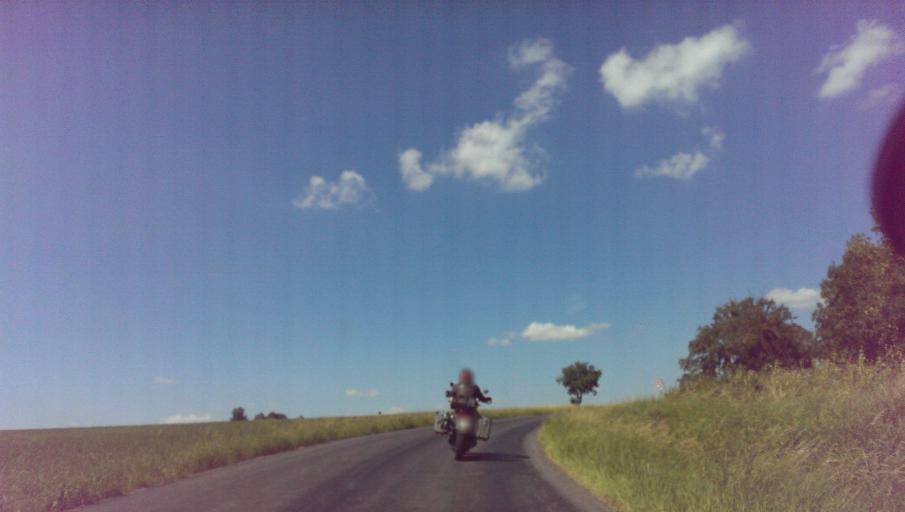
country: CZ
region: Moravskoslezsky
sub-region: Okres Novy Jicin
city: Pribor
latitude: 49.6283
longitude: 18.1798
